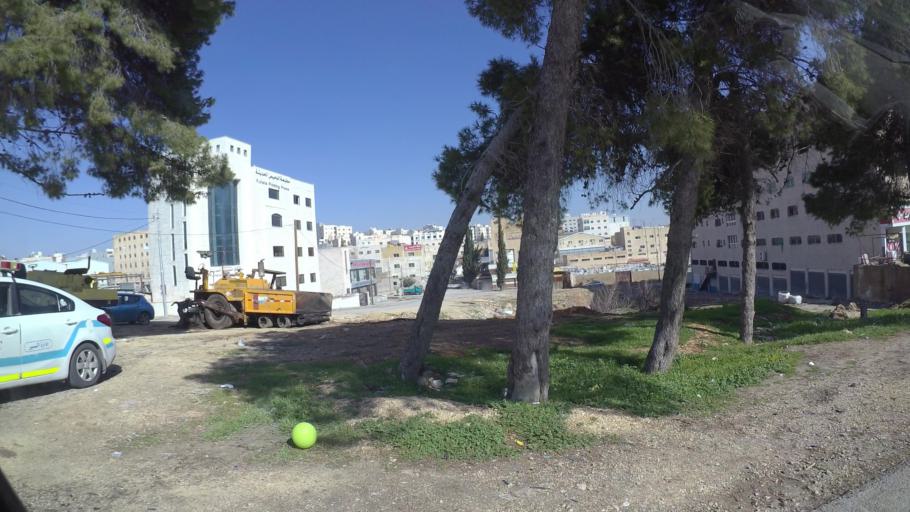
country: JO
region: Amman
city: Al Bunayyat ash Shamaliyah
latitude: 31.9108
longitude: 35.8946
